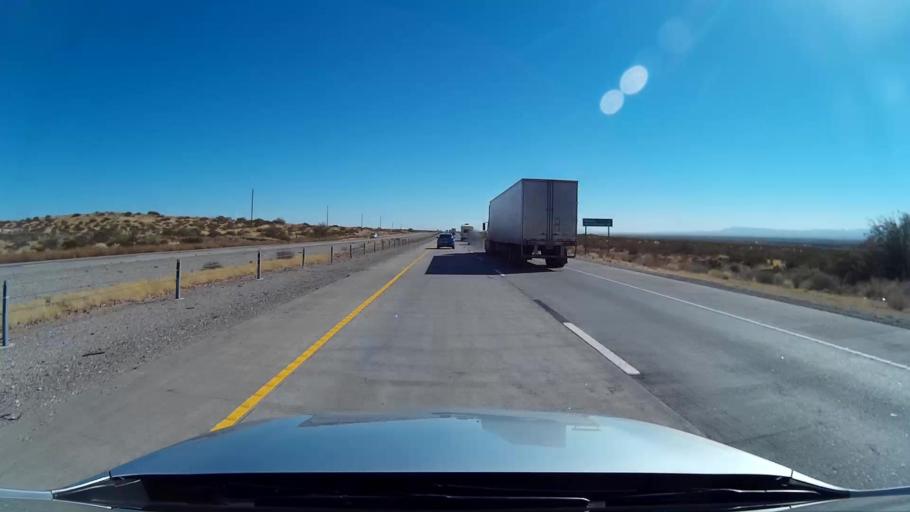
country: US
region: Texas
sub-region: El Paso County
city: Agua Dulce
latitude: 31.5884
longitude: -106.1847
